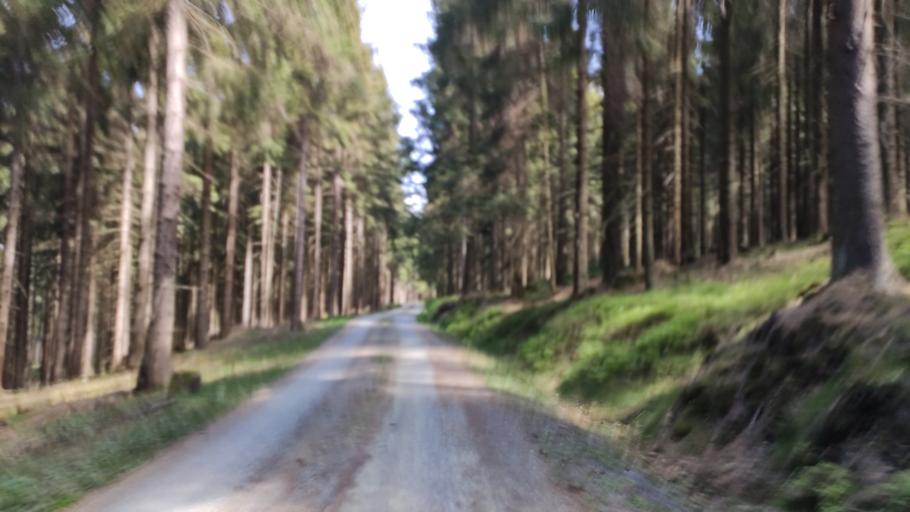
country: DE
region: Bavaria
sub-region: Upper Franconia
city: Reichenbach
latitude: 50.4522
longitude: 11.4491
